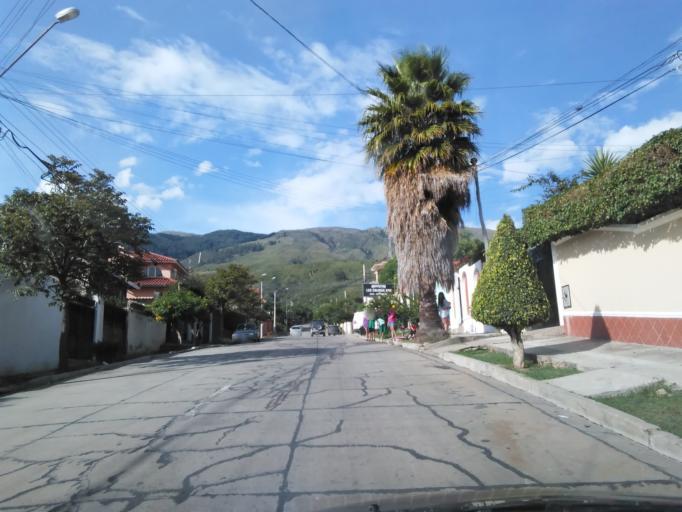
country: BO
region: Cochabamba
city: Cochabamba
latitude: -17.3658
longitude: -66.1451
